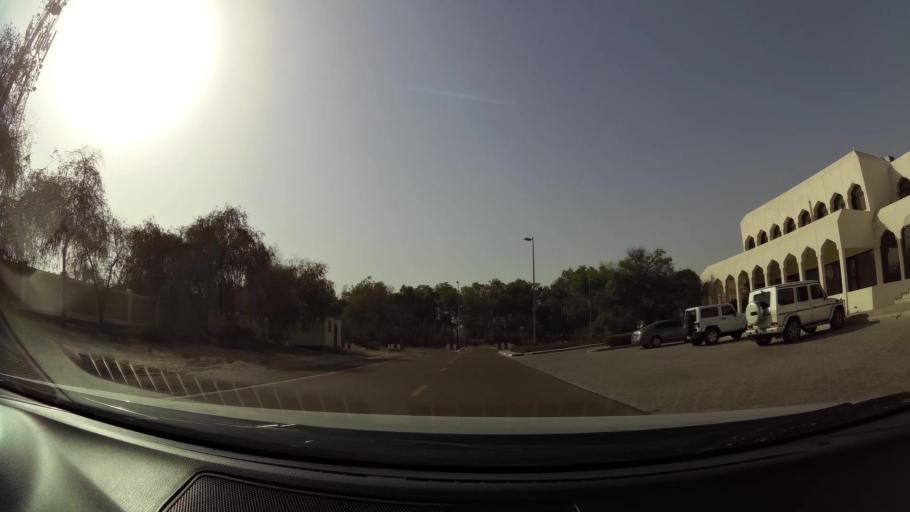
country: AE
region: Dubai
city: Dubai
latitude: 25.1552
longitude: 55.3233
